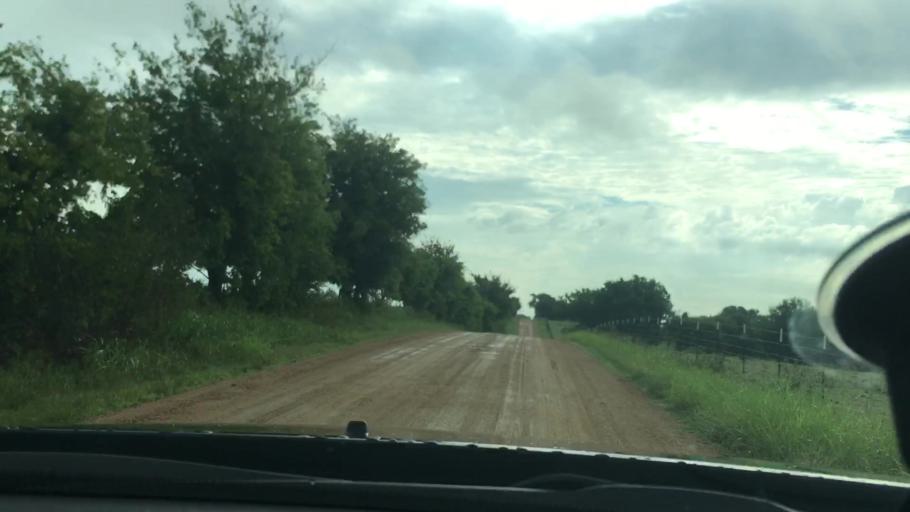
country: US
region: Oklahoma
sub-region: Johnston County
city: Tishomingo
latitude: 34.2888
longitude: -96.7804
